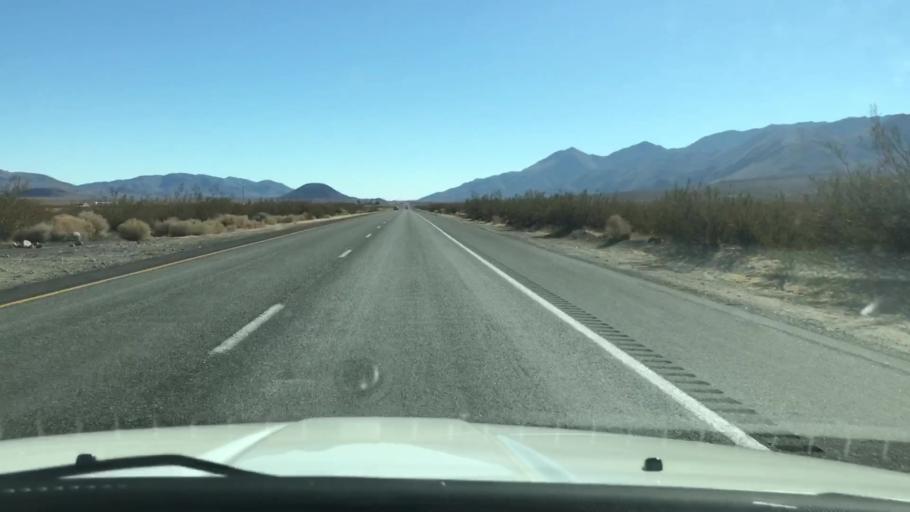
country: US
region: California
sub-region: Kern County
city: Inyokern
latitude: 36.0665
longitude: -117.9546
